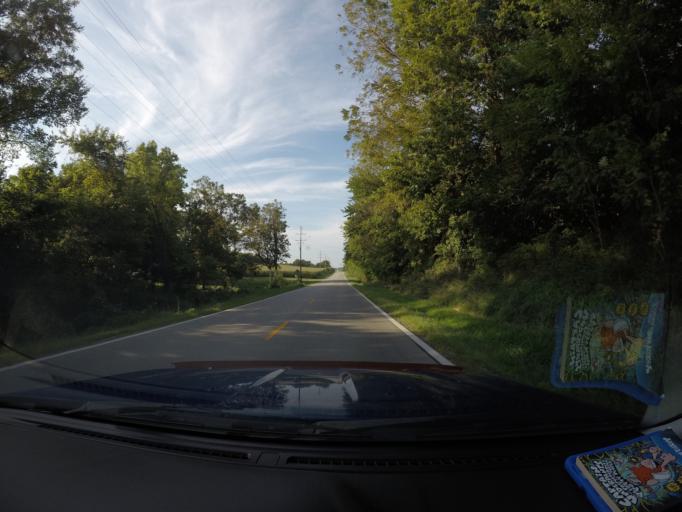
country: US
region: Kansas
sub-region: Atchison County
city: Atchison
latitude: 39.5889
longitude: -95.1340
